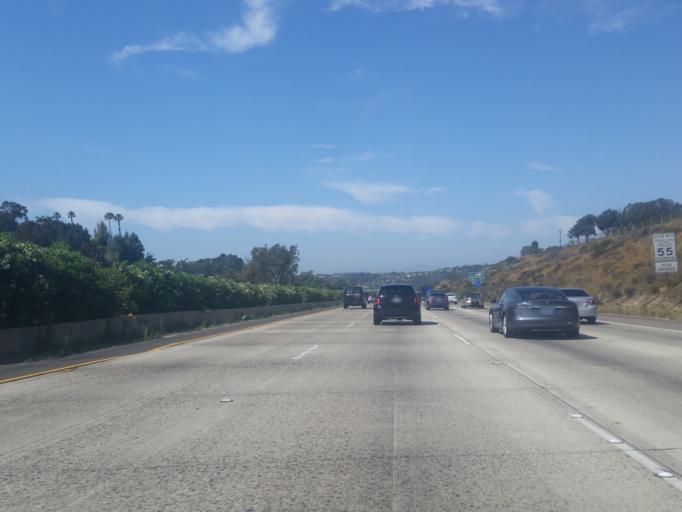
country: US
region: California
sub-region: San Diego County
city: Encinitas
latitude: 33.0759
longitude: -117.2954
